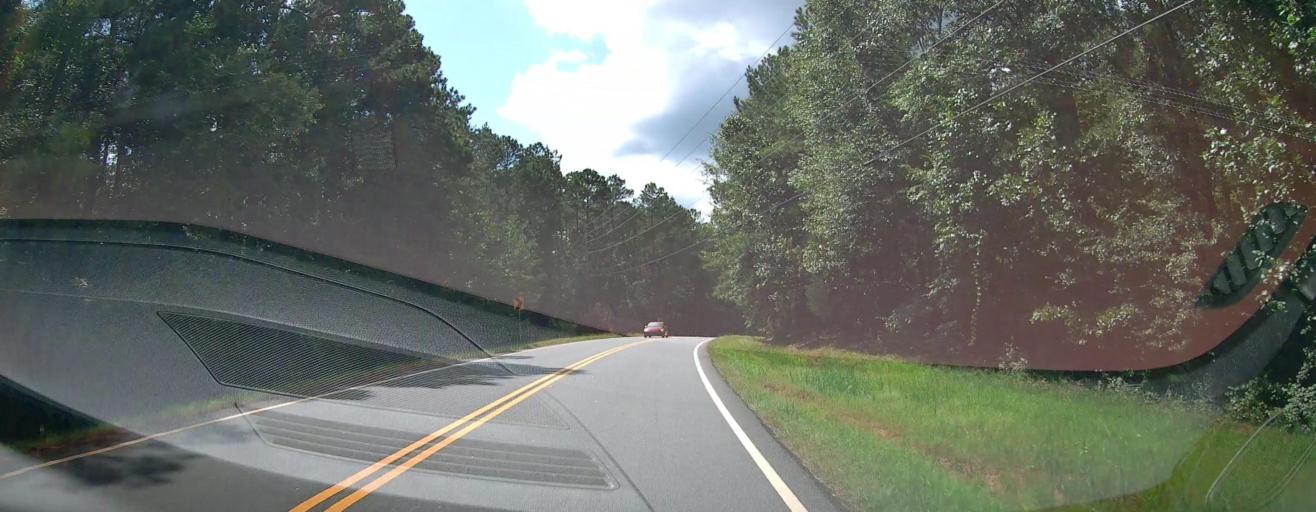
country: US
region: Georgia
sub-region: Monroe County
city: Forsyth
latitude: 32.8792
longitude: -83.9574
